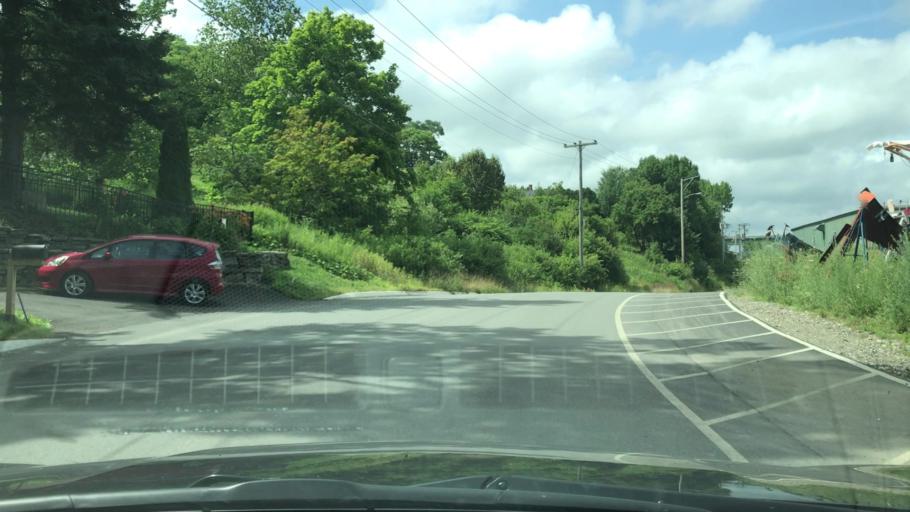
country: US
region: Maine
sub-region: Waldo County
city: Belfast
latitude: 44.4285
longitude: -69.0088
